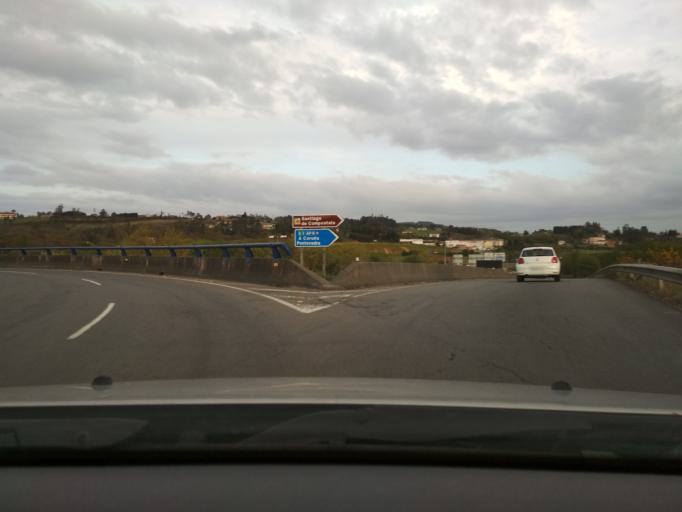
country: ES
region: Galicia
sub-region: Provincia da Coruna
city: Santiago de Compostela
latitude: 42.8984
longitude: -8.5103
